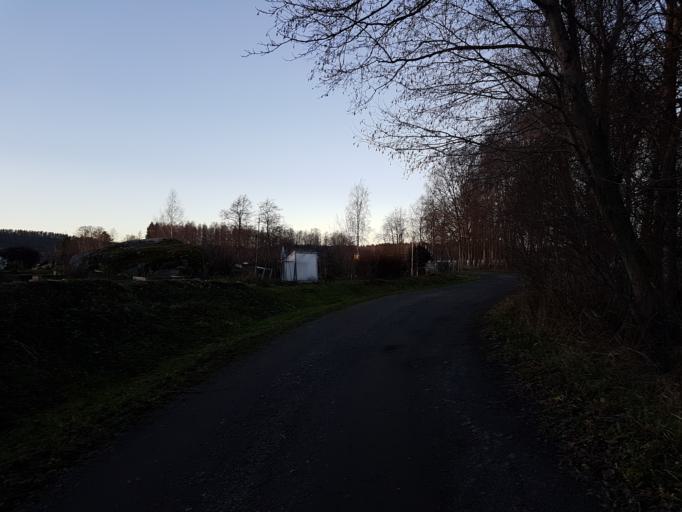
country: FI
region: Northern Savo
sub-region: Kuopio
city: Kuopio
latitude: 62.9295
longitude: 27.6258
